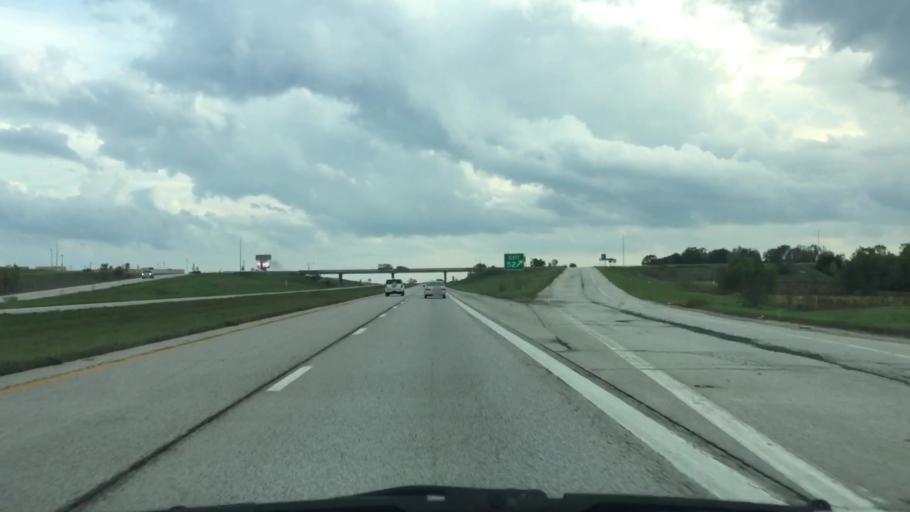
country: US
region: Missouri
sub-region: Clinton County
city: Cameron
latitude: 39.7347
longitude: -94.2206
